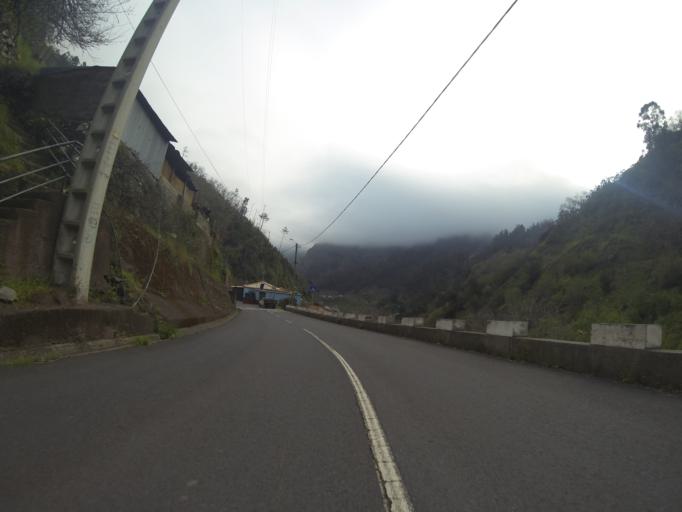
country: PT
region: Madeira
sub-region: Camara de Lobos
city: Curral das Freiras
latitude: 32.7396
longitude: -16.9686
